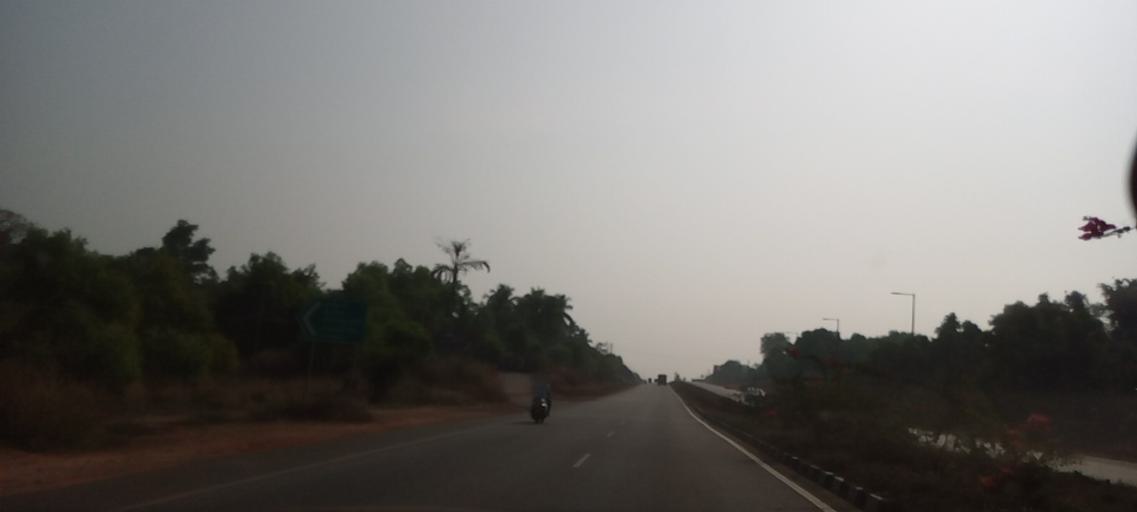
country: IN
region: Karnataka
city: Gangolli
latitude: 13.6884
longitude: 74.6647
